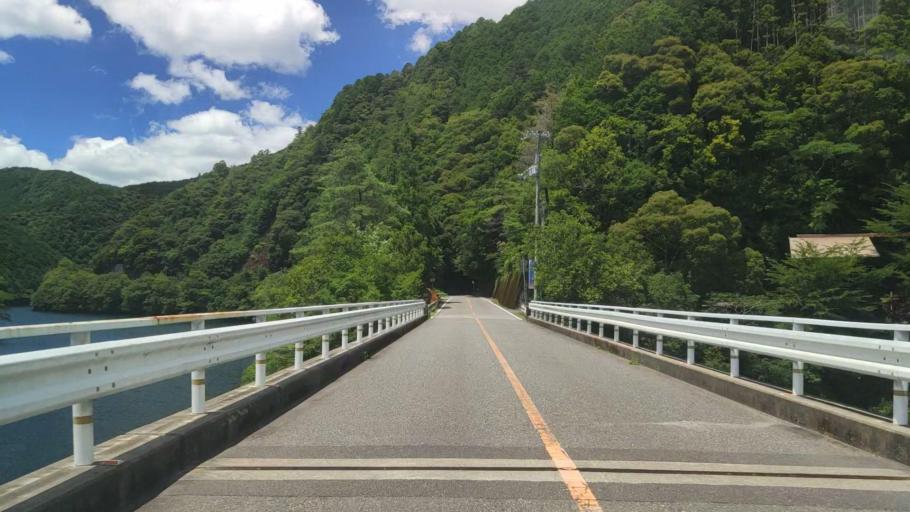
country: JP
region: Mie
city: Owase
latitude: 33.9976
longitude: 136.0226
